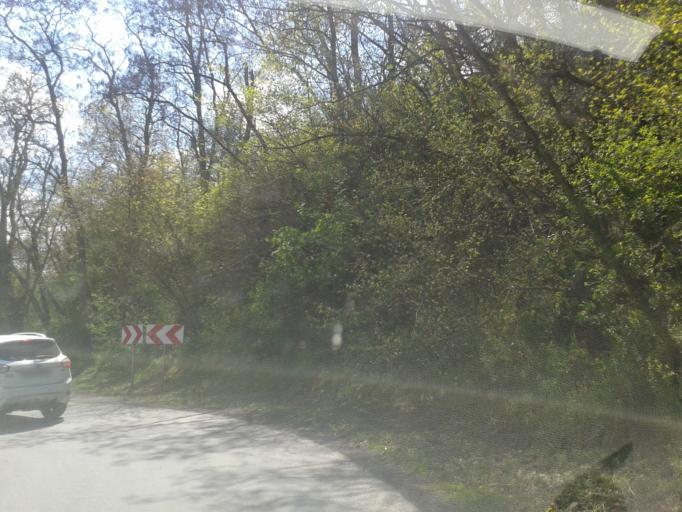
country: CZ
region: Central Bohemia
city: Nizbor
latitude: 49.9978
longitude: 13.9950
